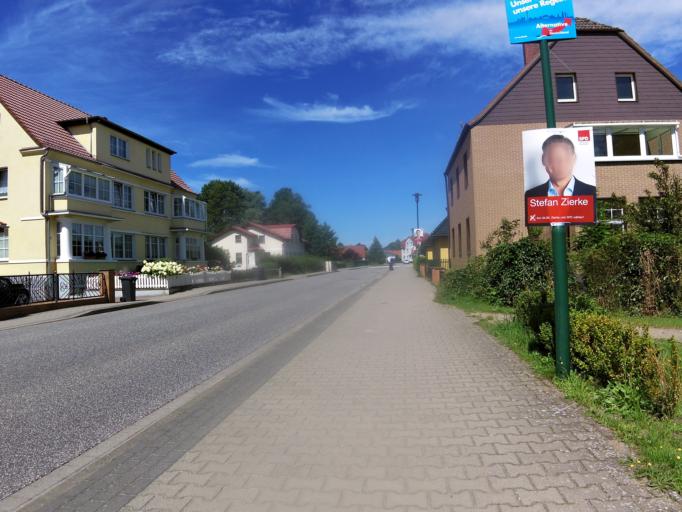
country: DE
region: Brandenburg
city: Lychen
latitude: 53.2112
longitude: 13.3046
